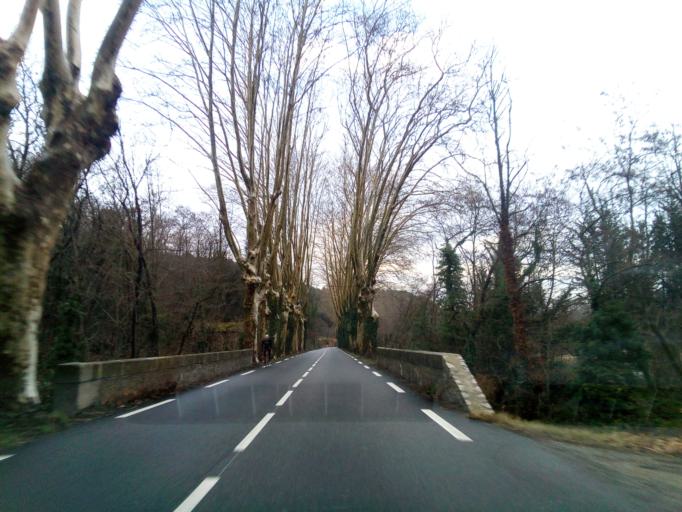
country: FR
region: Rhone-Alpes
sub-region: Departement de l'Ardeche
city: Saint-Laurent-du-Pape
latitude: 44.8236
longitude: 4.7319
